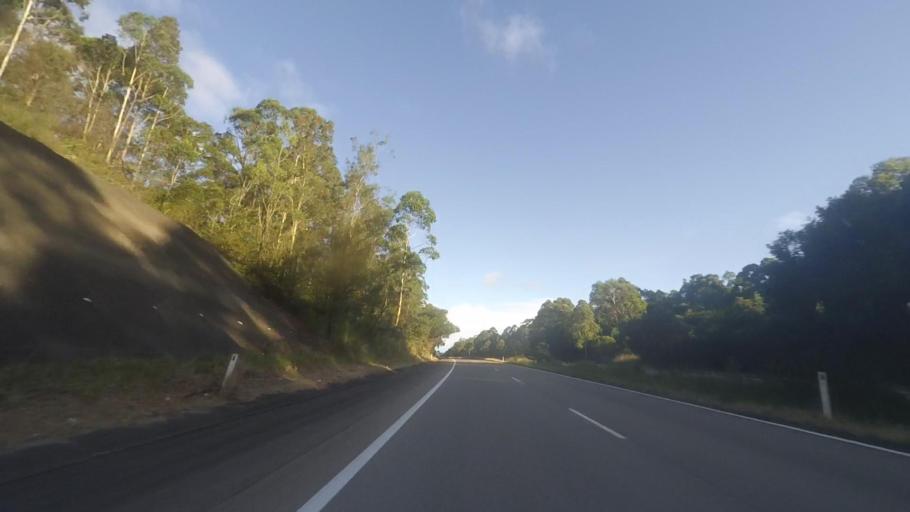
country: AU
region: New South Wales
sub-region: Great Lakes
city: Bulahdelah
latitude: -32.2788
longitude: 152.3319
